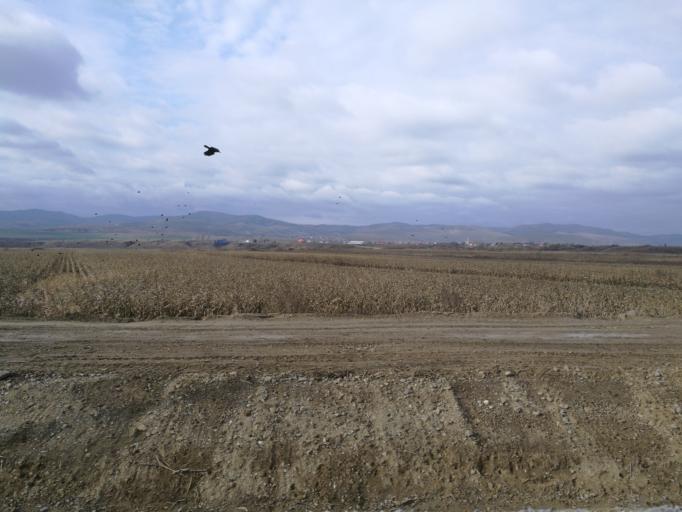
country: RO
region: Bacau
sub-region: Comuna Nicolae Balcescu
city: Galbeni
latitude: 46.4644
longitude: 26.9343
